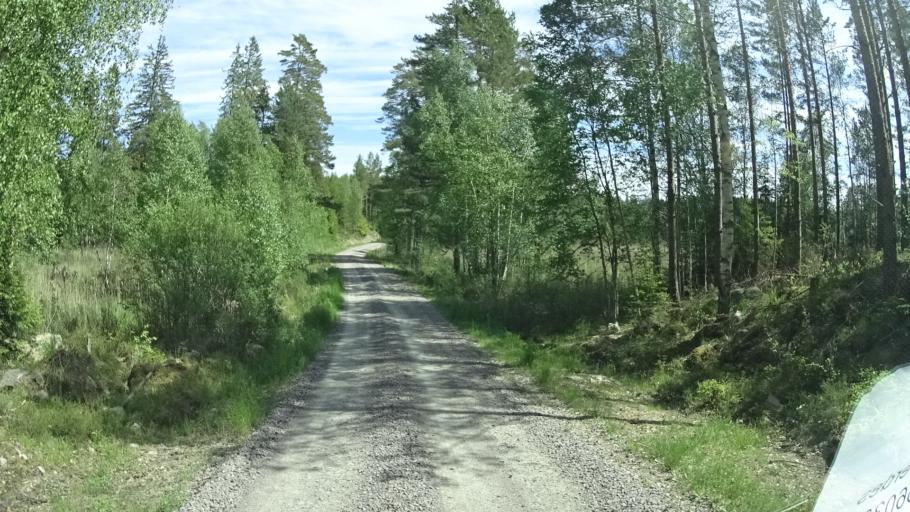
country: SE
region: OEstergoetland
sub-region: Norrkopings Kommun
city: Svartinge
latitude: 58.7808
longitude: 15.9214
